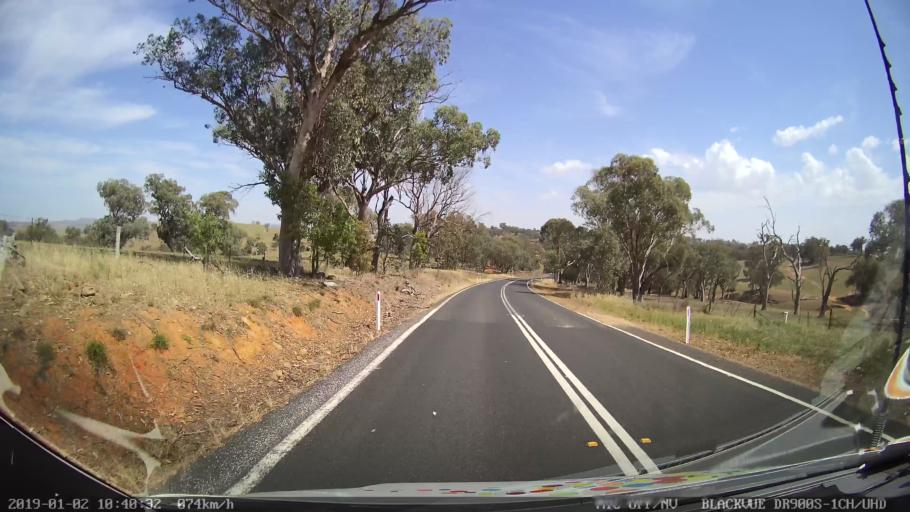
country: AU
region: New South Wales
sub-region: Cootamundra
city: Cootamundra
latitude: -34.8011
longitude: 148.3150
